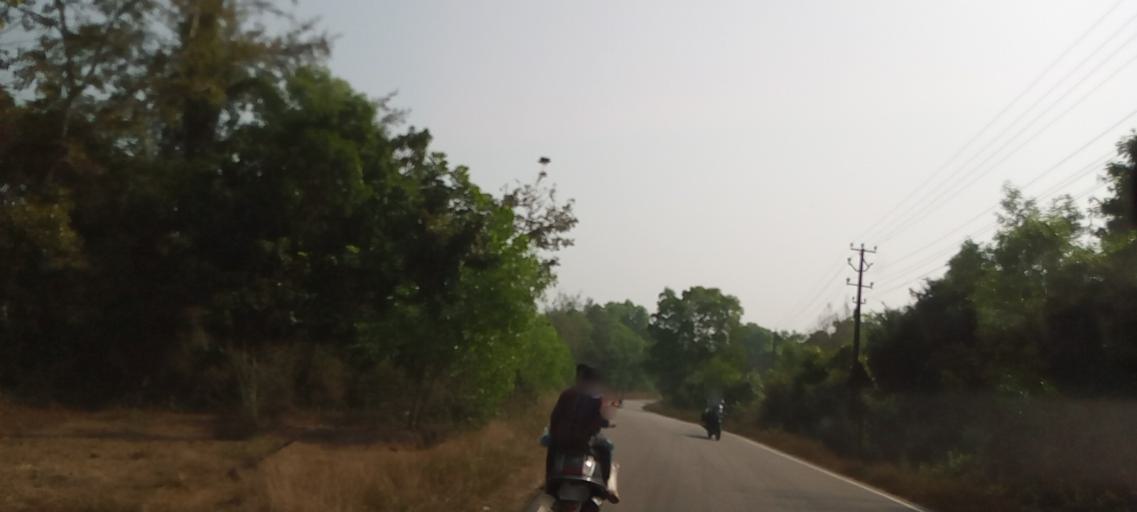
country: IN
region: Karnataka
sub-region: Udupi
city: Coondapoor
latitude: 13.5119
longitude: 74.7821
